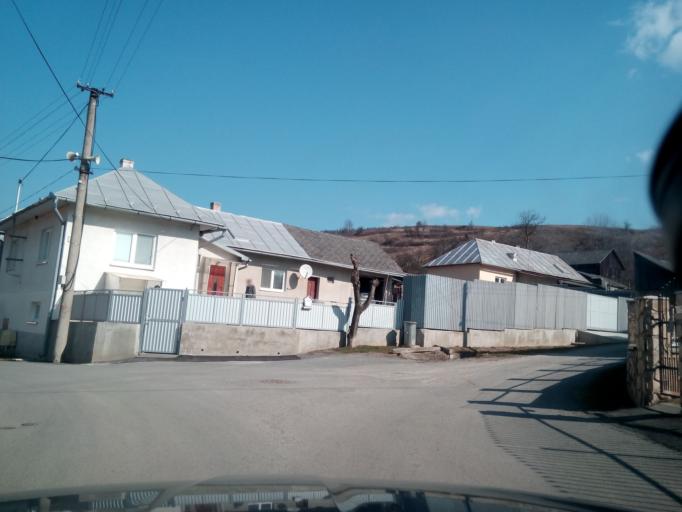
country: SK
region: Presovsky
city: Lipany
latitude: 49.1937
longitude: 20.9607
